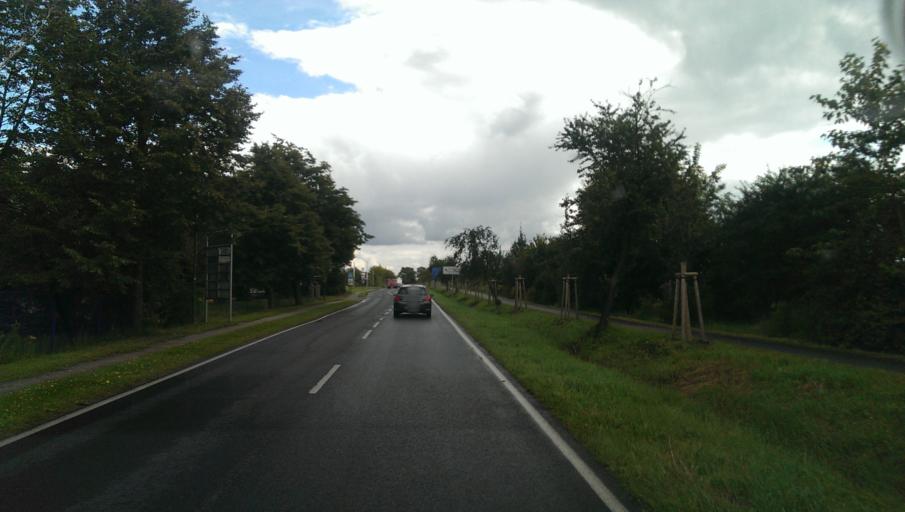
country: DE
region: Brandenburg
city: Velten
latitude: 52.6924
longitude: 13.1147
